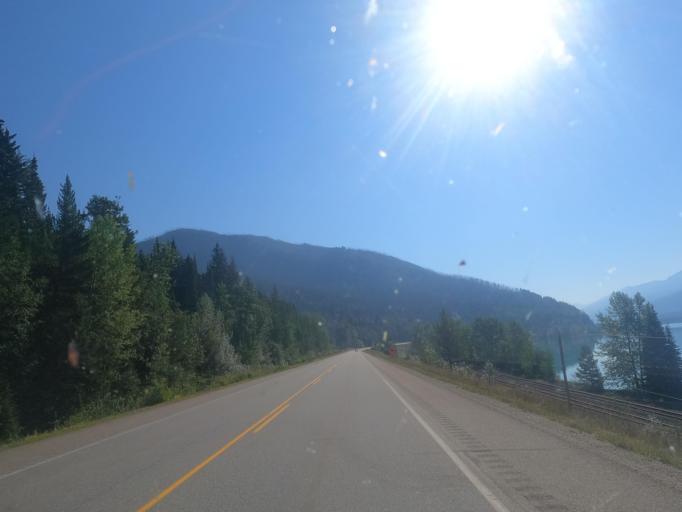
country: CA
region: Alberta
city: Jasper Park Lodge
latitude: 52.9532
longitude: -118.8743
